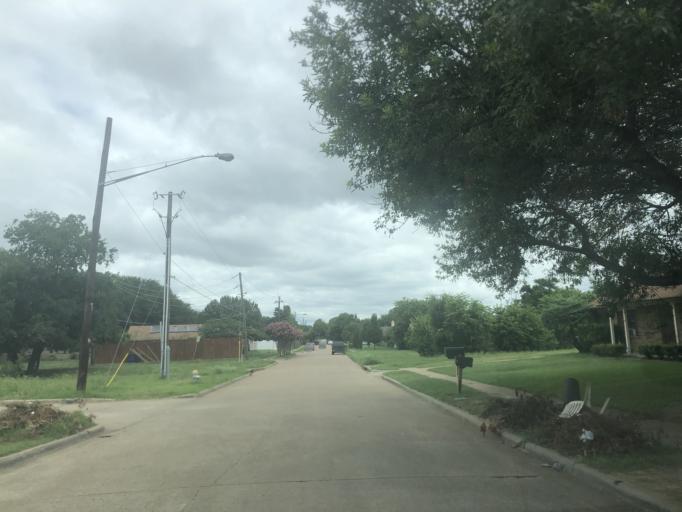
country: US
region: Texas
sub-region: Dallas County
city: Duncanville
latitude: 32.6374
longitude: -96.9437
